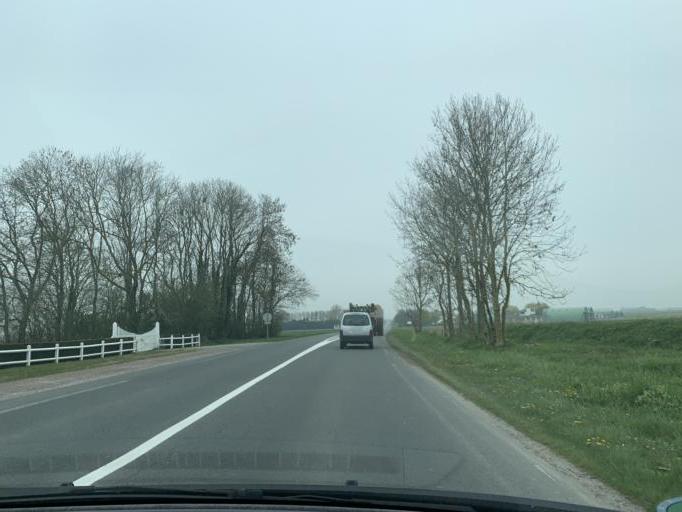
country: FR
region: Picardie
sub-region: Departement de la Somme
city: Abbeville
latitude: 50.1367
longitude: 1.8256
